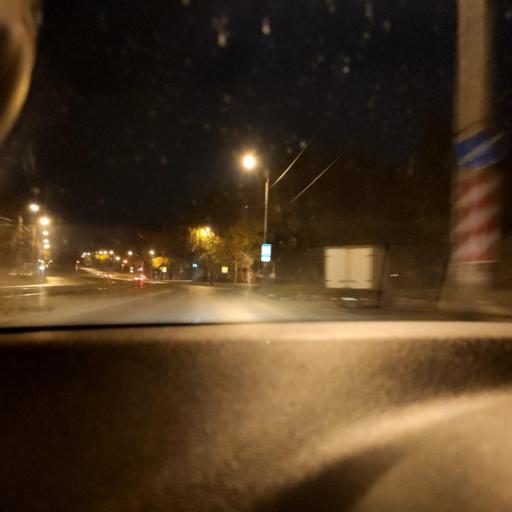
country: RU
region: Samara
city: Samara
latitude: 53.2250
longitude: 50.2333
